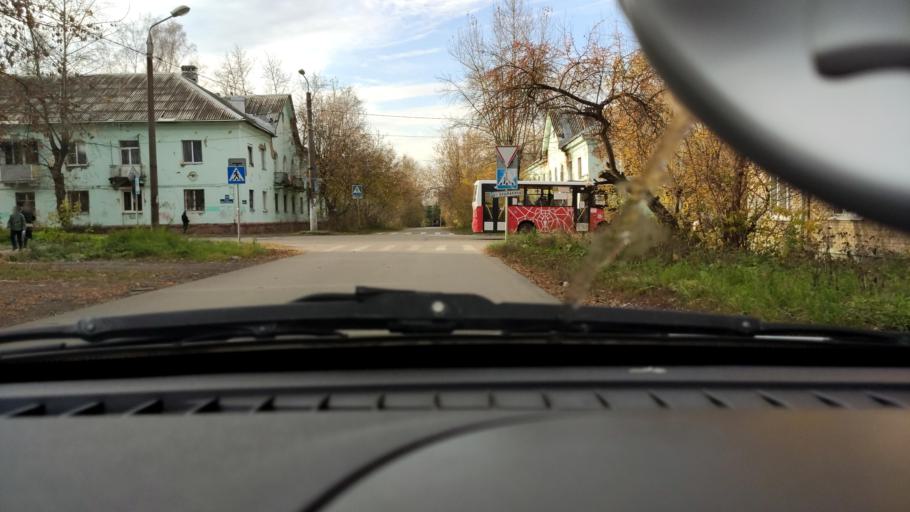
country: RU
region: Perm
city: Perm
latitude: 58.0875
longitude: 56.3906
